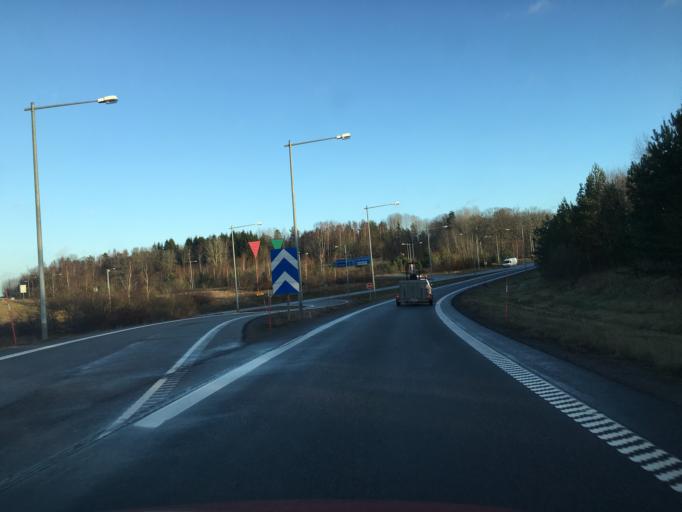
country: SE
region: Kalmar
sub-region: Vasterviks Kommun
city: Vaestervik
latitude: 57.7628
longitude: 16.5579
